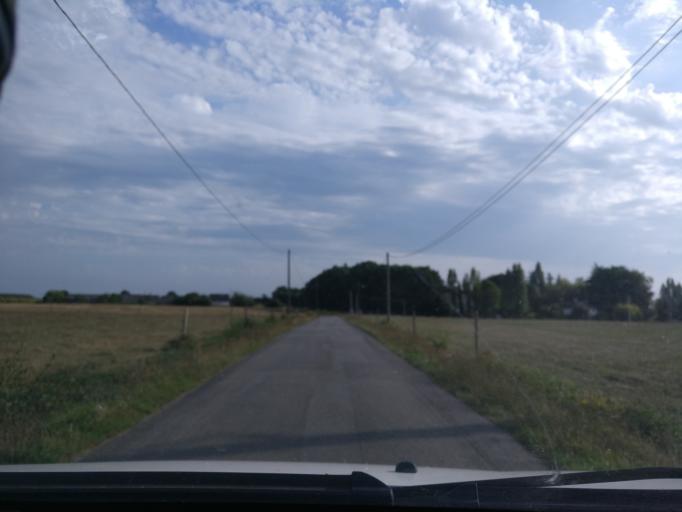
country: FR
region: Brittany
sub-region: Departement d'Ille-et-Vilaine
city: Cesson-Sevigne
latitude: 48.1297
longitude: -1.5804
